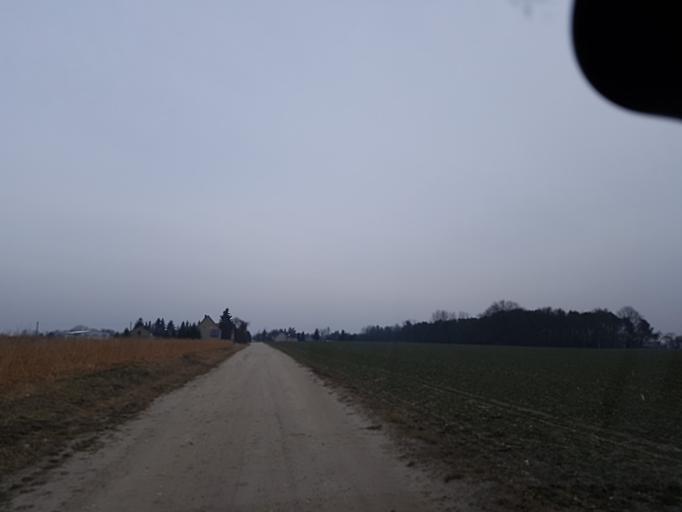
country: DE
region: Brandenburg
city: Ruckersdorf
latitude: 51.5873
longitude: 13.5435
